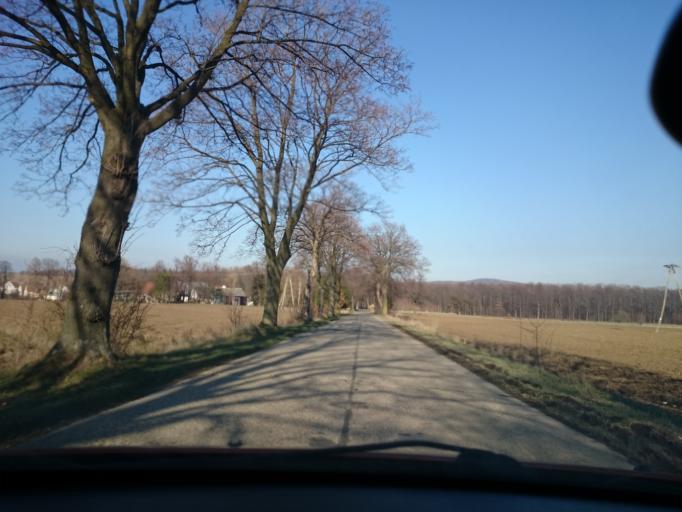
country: PL
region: Lower Silesian Voivodeship
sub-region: Powiat klodzki
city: Bystrzyca Klodzka
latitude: 50.3486
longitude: 16.5997
